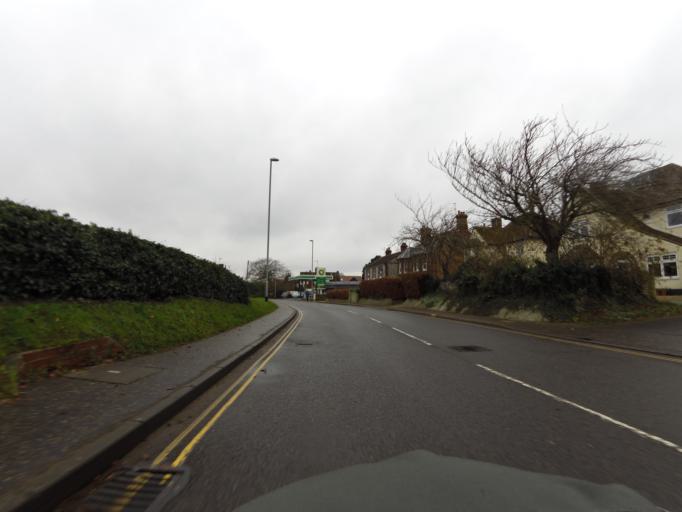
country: GB
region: England
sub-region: Norfolk
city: Briston
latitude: 52.9075
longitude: 1.0942
